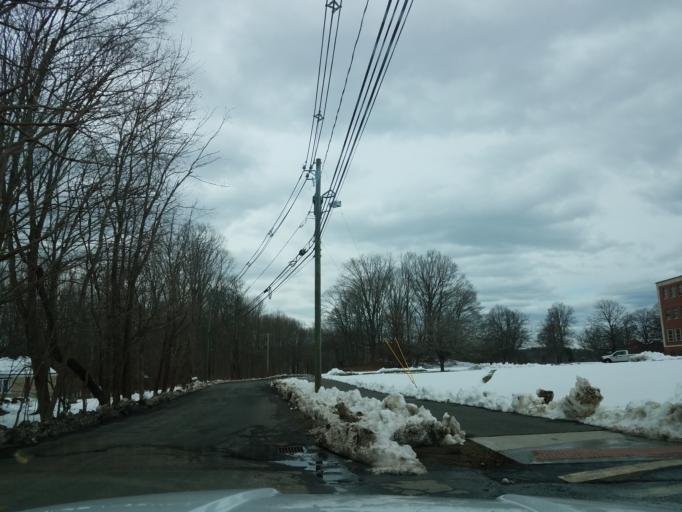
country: US
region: Connecticut
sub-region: Fairfield County
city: Newtown
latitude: 41.3980
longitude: -73.2879
